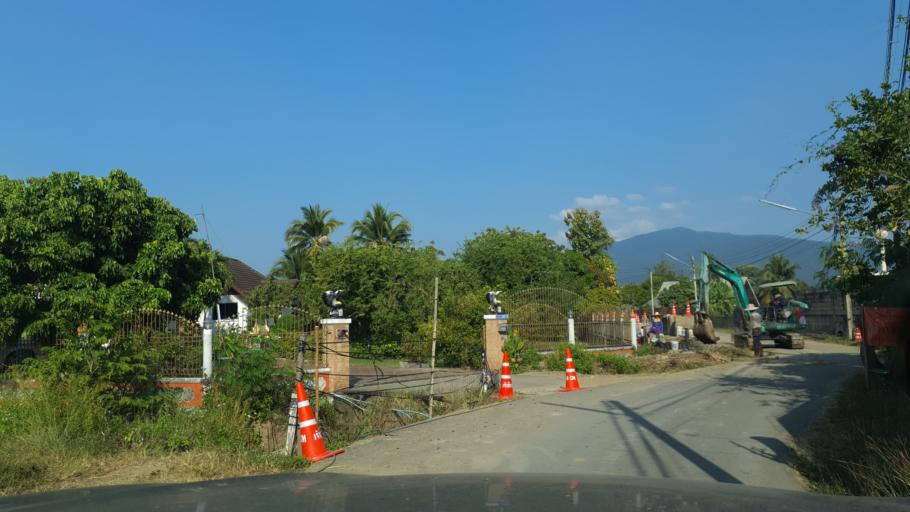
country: TH
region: Chiang Mai
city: Hang Dong
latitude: 18.7261
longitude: 98.9401
